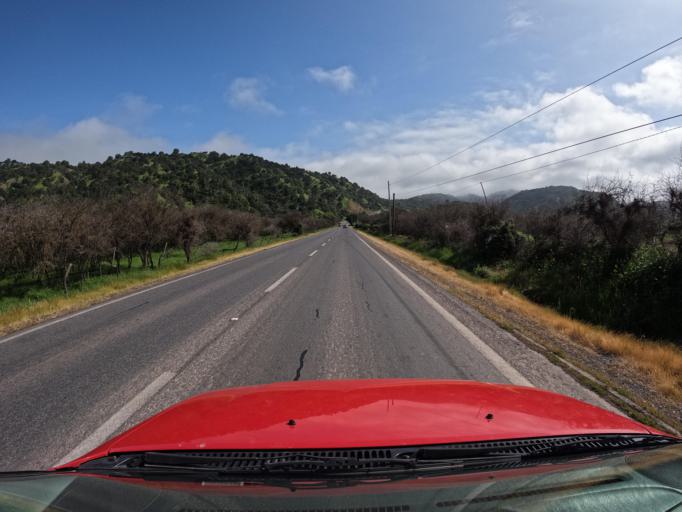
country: CL
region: Maule
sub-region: Provincia de Curico
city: Teno
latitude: -34.8264
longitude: -71.1915
